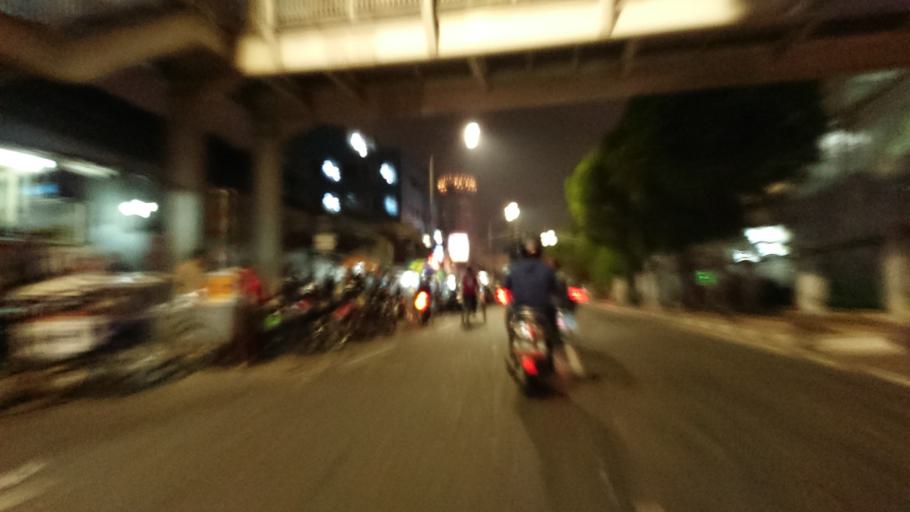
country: ID
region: Jakarta Raya
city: Jakarta
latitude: -6.2081
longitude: 106.7969
